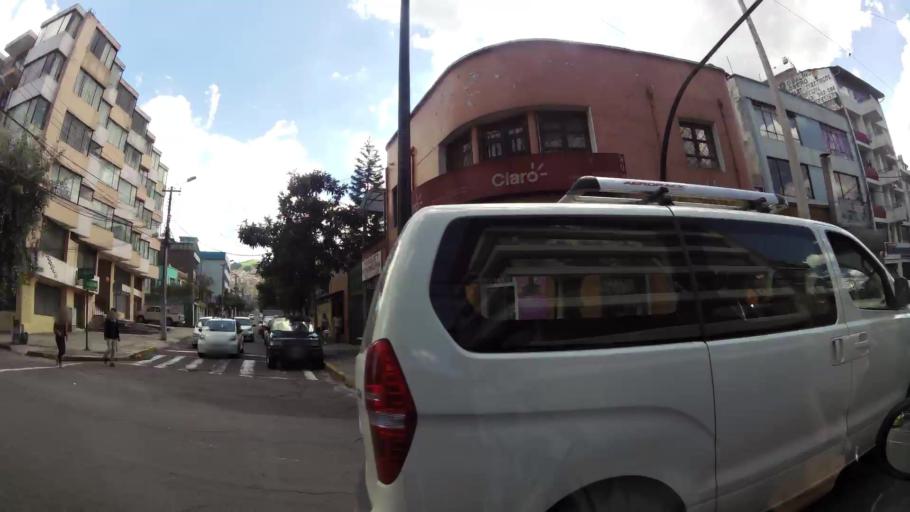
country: EC
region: Pichincha
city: Quito
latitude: -0.2059
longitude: -78.5028
